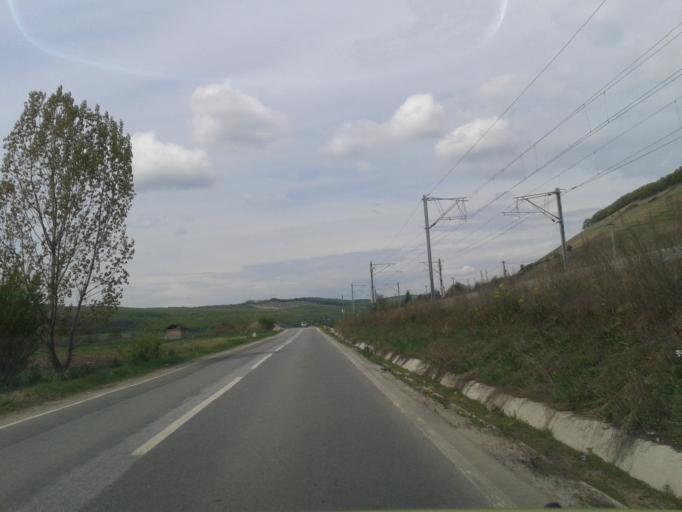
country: RO
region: Sibiu
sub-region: Comuna Micasasa
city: Micasasa
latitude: 46.0860
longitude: 24.0856
